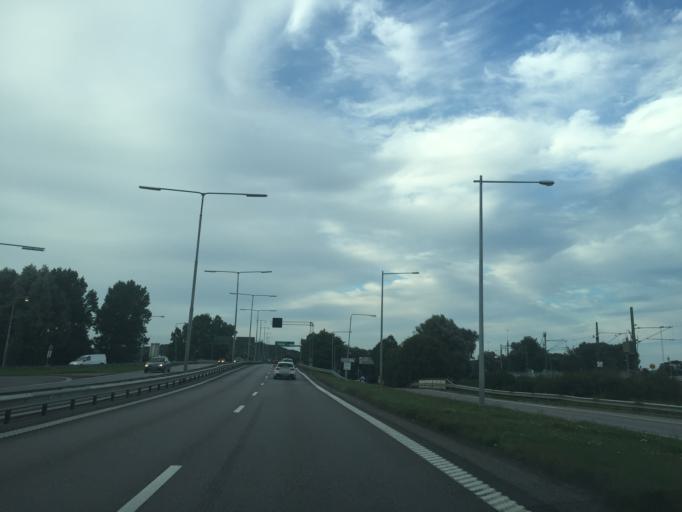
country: SE
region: Vaestra Goetaland
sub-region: Goteborg
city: Goeteborg
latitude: 57.7188
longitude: 11.9541
